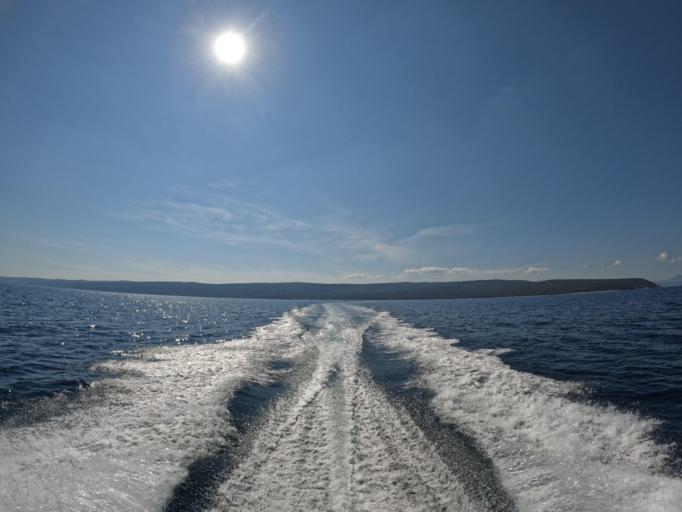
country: HR
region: Primorsko-Goranska
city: Cres
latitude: 44.9454
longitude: 14.5054
